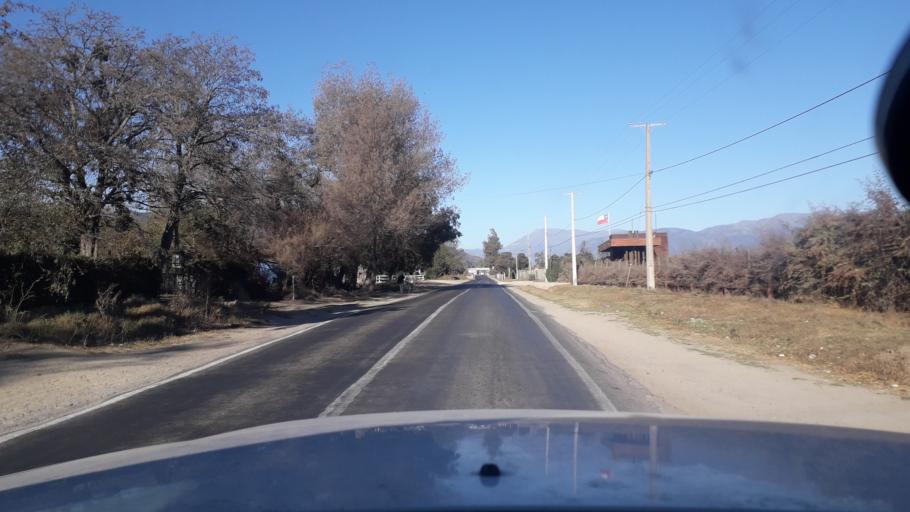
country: CL
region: Valparaiso
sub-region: Provincia de Marga Marga
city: Limache
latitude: -32.9692
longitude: -71.3081
